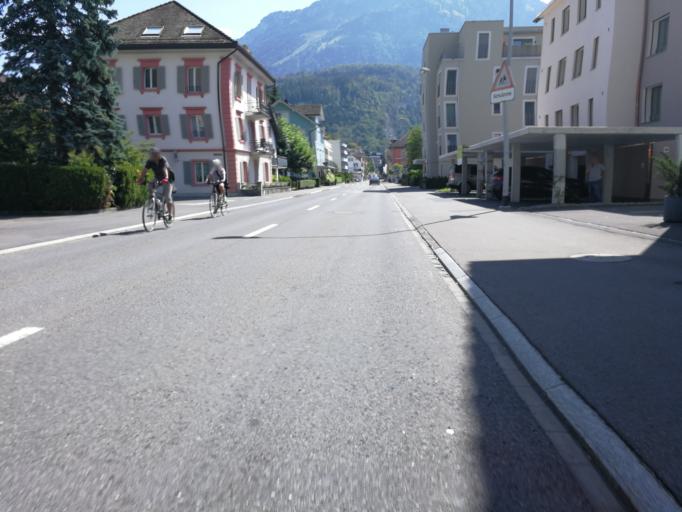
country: CH
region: Schwyz
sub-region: Bezirk Schwyz
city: Ingenbohl
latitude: 46.9968
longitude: 8.6002
